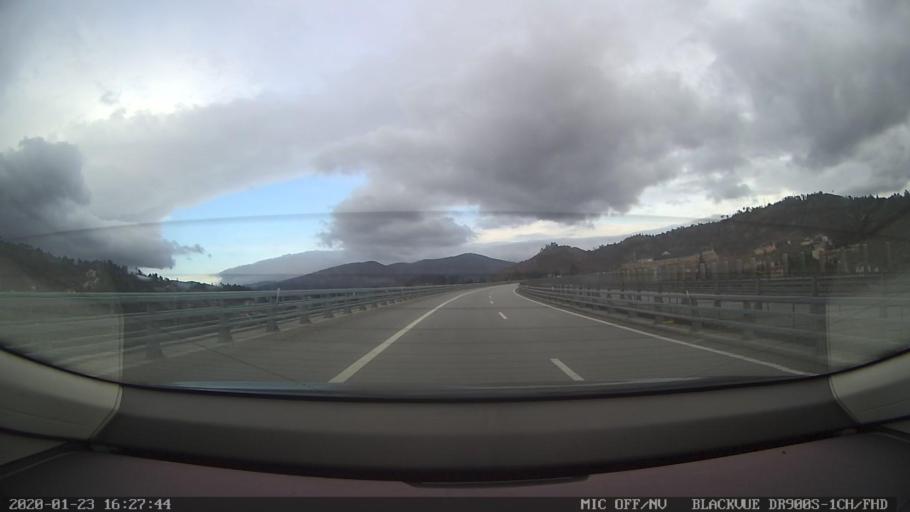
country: PT
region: Porto
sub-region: Amarante
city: Amarante
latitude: 41.2604
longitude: -8.0266
